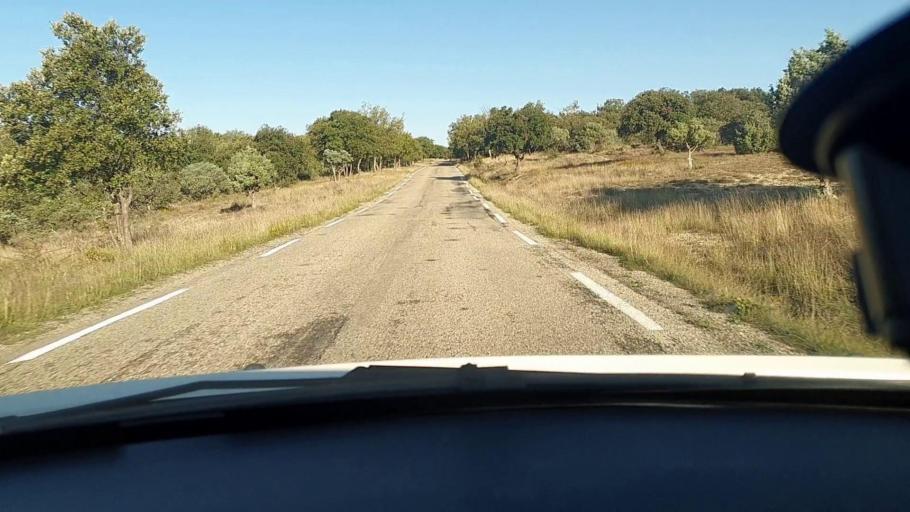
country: FR
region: Languedoc-Roussillon
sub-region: Departement du Gard
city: Barjac
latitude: 44.1651
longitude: 4.3308
